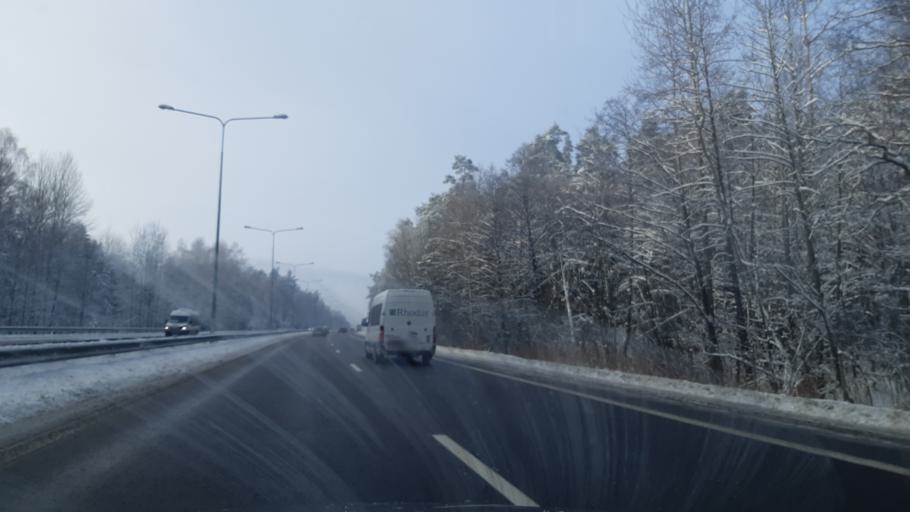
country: LT
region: Kauno apskritis
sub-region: Kauno rajonas
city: Karmelava
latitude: 54.8892
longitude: 24.1697
